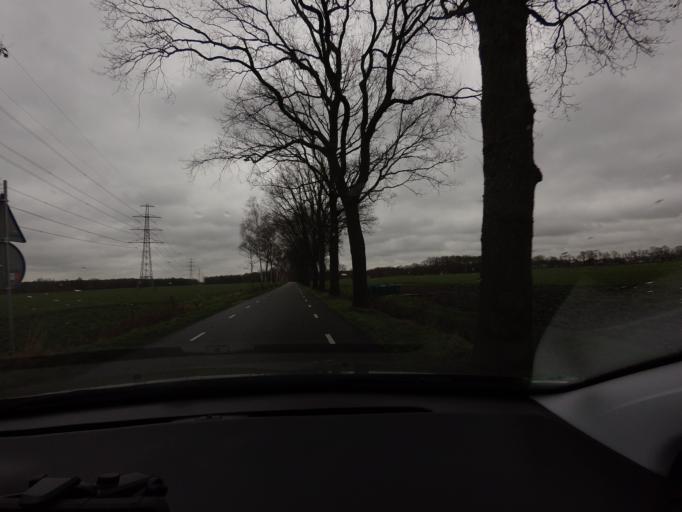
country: NL
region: Drenthe
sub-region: Gemeente Hoogeveen
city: Hoogeveen
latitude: 52.7595
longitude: 6.4893
